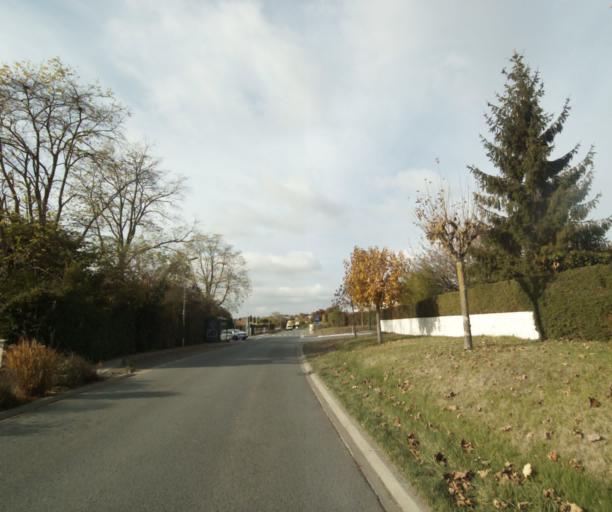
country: FR
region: Poitou-Charentes
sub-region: Departement de la Charente-Maritime
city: Saint-Georges-des-Coteaux
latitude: 45.7640
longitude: -0.7004
